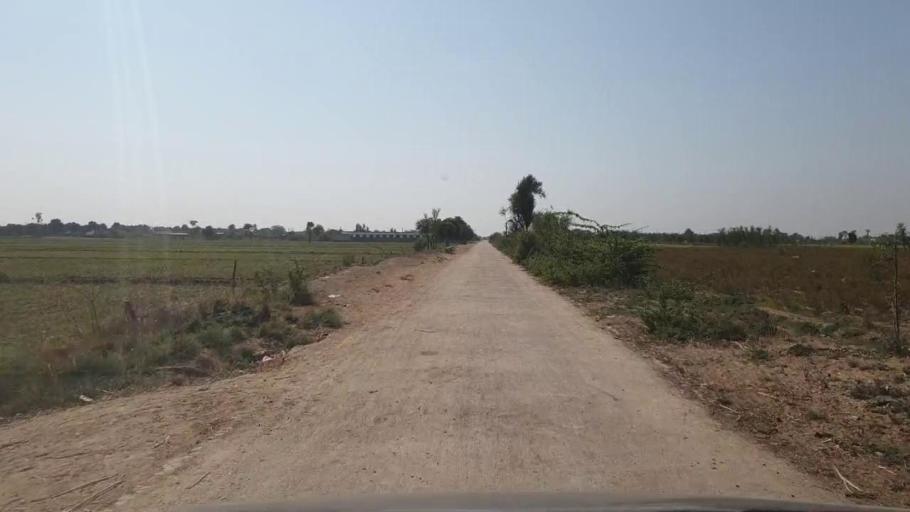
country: PK
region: Sindh
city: Samaro
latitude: 25.2351
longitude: 69.2600
